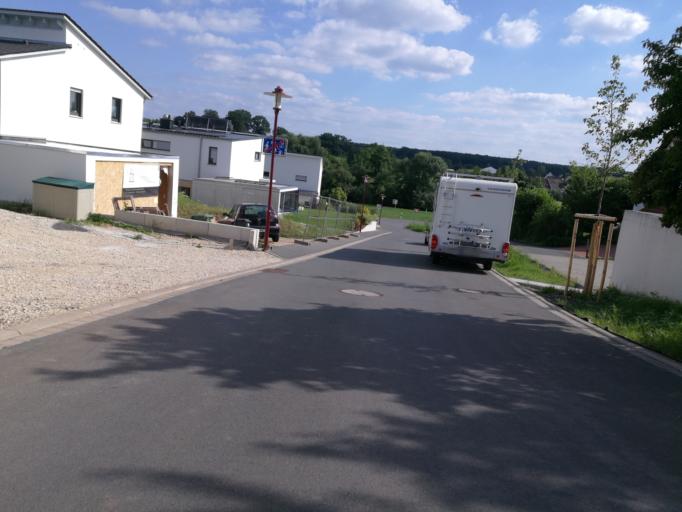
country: DE
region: Bavaria
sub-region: Regierungsbezirk Mittelfranken
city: Veitsbronn
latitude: 49.5092
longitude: 10.8954
